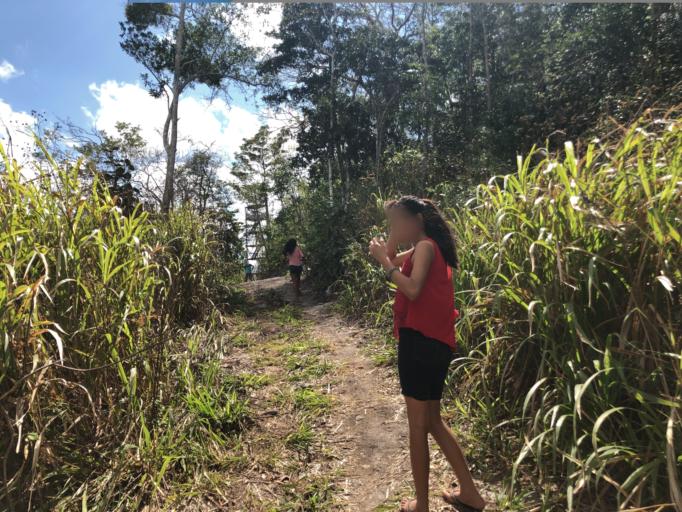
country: MX
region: Quintana Roo
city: Nicolas Bravo
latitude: 18.4461
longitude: -89.3112
